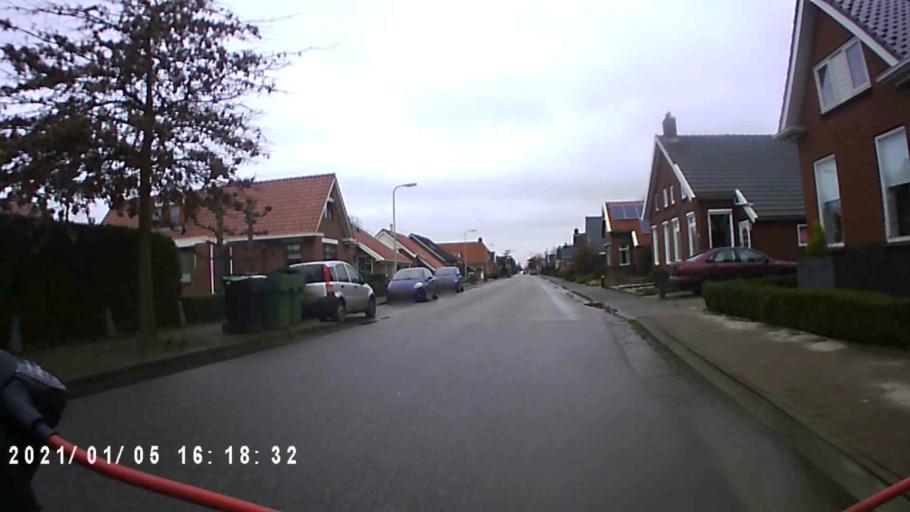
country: NL
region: Groningen
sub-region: Gemeente  Oldambt
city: Winschoten
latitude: 53.1963
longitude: 7.0500
